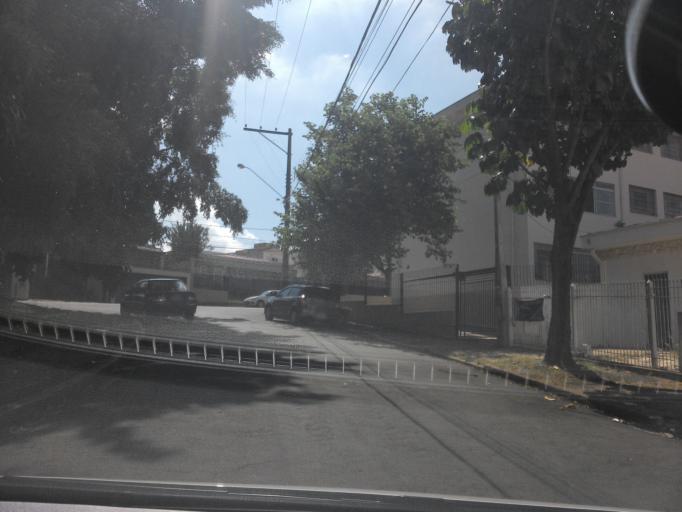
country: BR
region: Sao Paulo
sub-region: Campinas
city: Campinas
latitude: -22.8818
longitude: -47.0710
